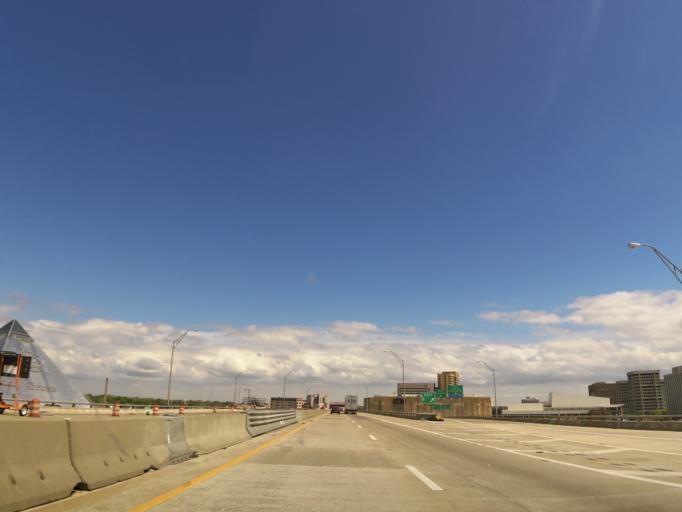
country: US
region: Tennessee
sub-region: Shelby County
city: Memphis
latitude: 35.1531
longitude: -90.0571
